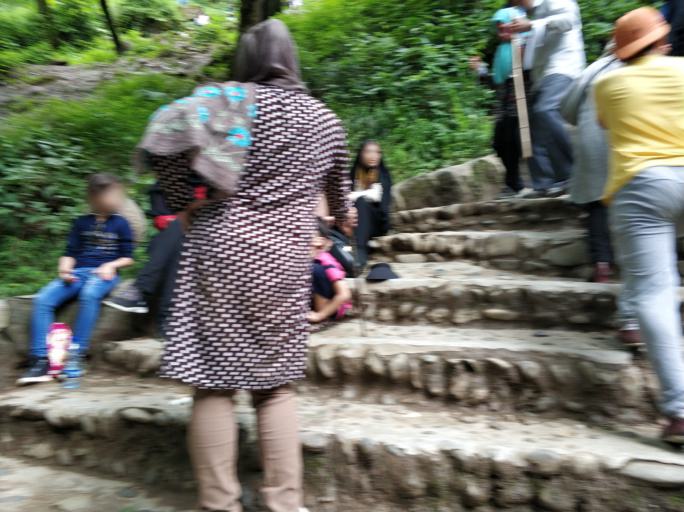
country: IR
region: Gilan
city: Fuman
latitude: 37.0683
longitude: 49.2431
